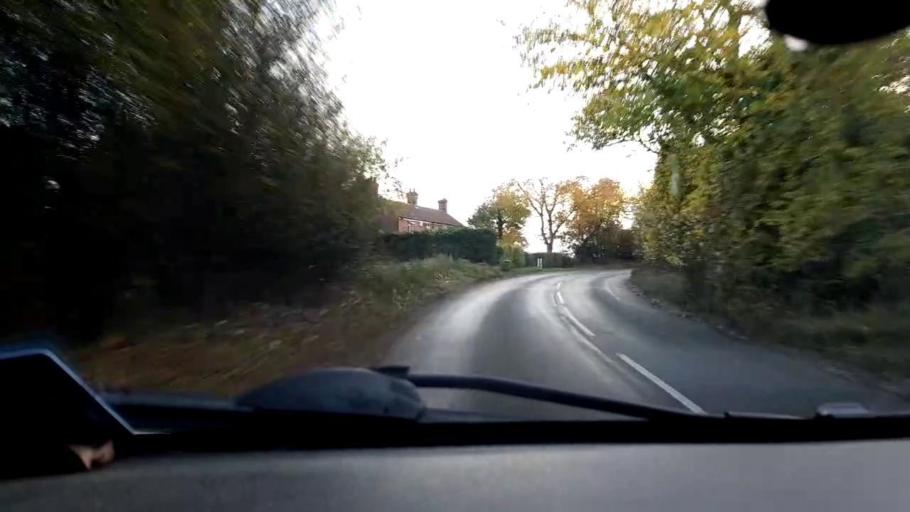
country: GB
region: England
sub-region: Norfolk
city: Mattishall
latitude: 52.7074
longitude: 1.1054
